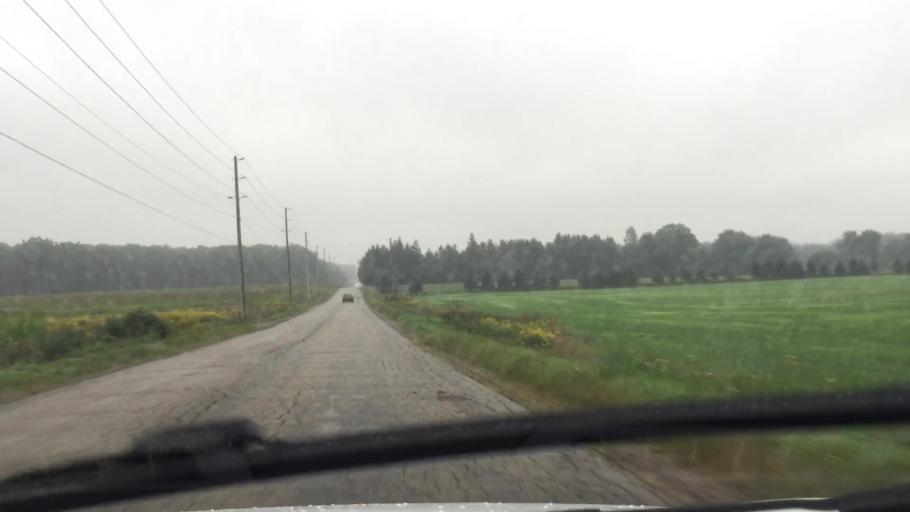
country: CA
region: Ontario
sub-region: Oxford County
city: Woodstock
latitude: 43.1113
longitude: -80.7139
